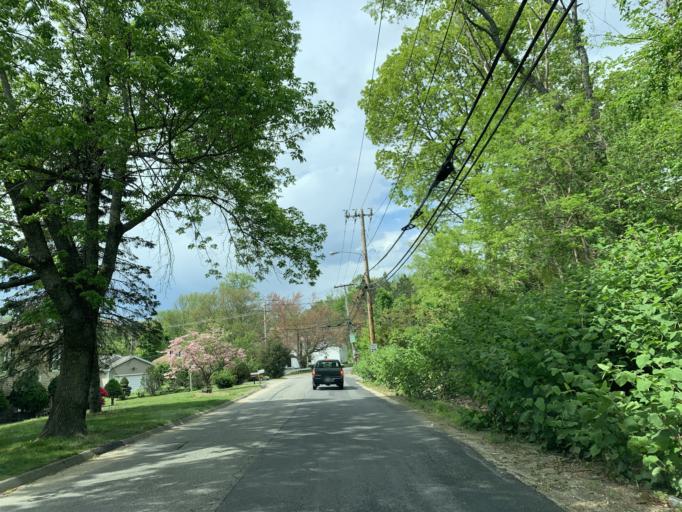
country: US
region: Rhode Island
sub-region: Providence County
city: Johnston
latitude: 41.8045
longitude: -71.4759
